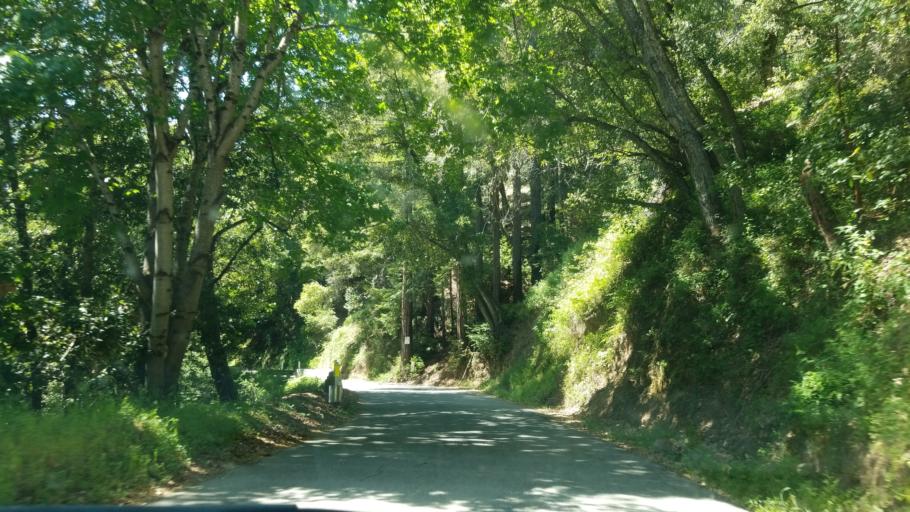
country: US
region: California
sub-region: Santa Cruz County
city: Day Valley
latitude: 37.0555
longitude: -121.8153
